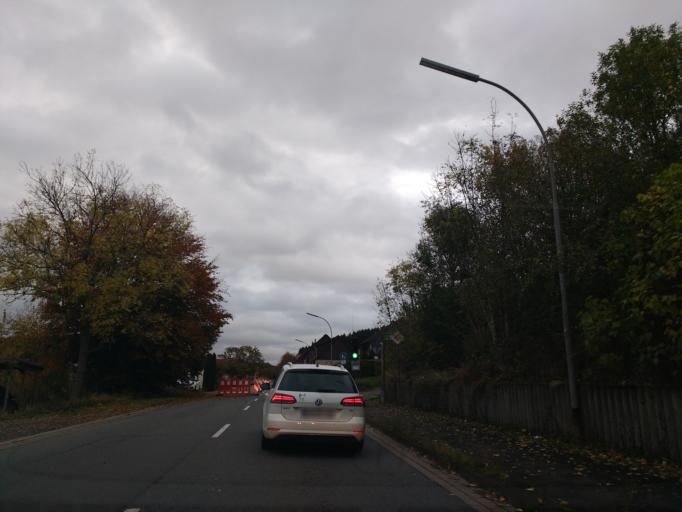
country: DE
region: Lower Saxony
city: Bad Lauterberg im Harz
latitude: 51.6095
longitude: 10.4342
